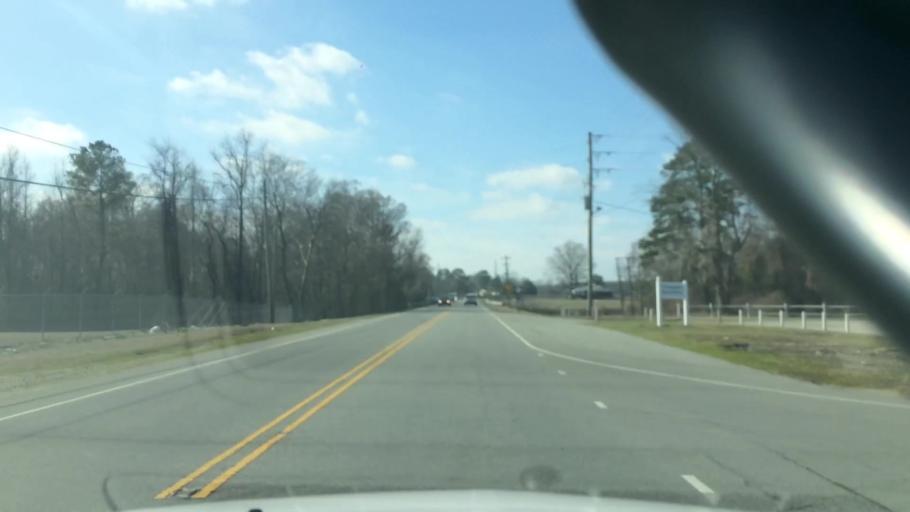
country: US
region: North Carolina
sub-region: Duplin County
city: Wallace
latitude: 34.7853
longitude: -77.9033
